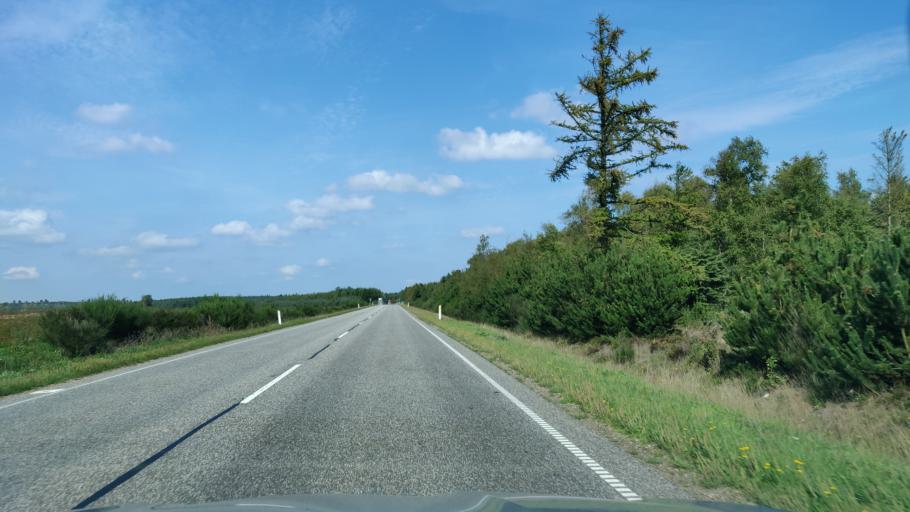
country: DK
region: Central Jutland
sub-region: Herning Kommune
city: Sunds
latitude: 56.3456
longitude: 8.9769
